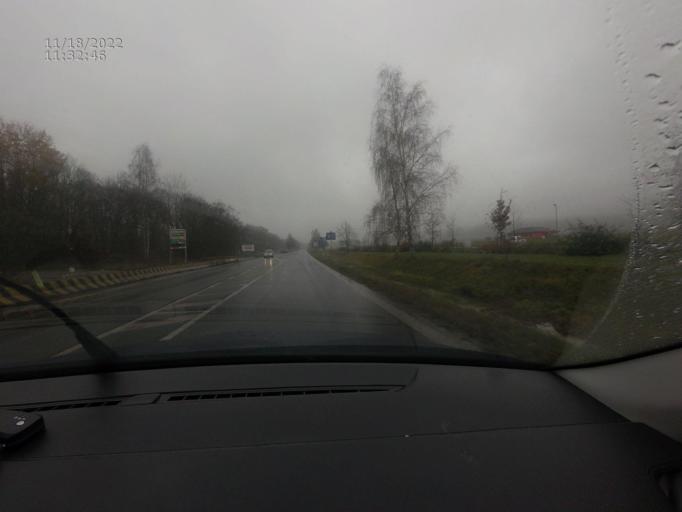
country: CZ
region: Plzensky
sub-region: Okres Rokycany
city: Rokycany
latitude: 49.7301
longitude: 13.5856
